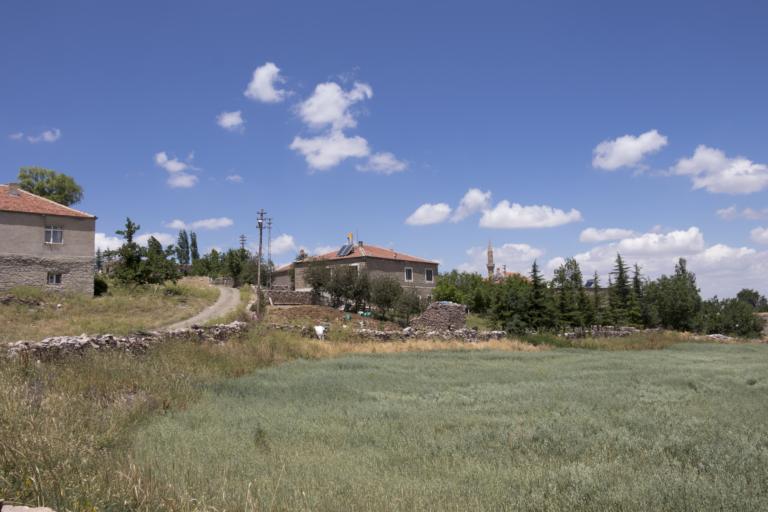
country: TR
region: Kayseri
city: Toklar
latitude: 38.4197
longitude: 36.0957
